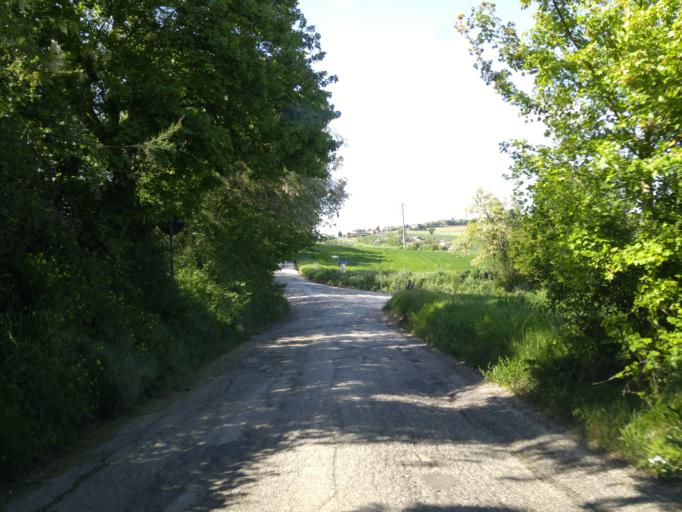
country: IT
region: The Marches
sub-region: Provincia di Pesaro e Urbino
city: Cartoceto
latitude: 43.7809
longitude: 12.9032
